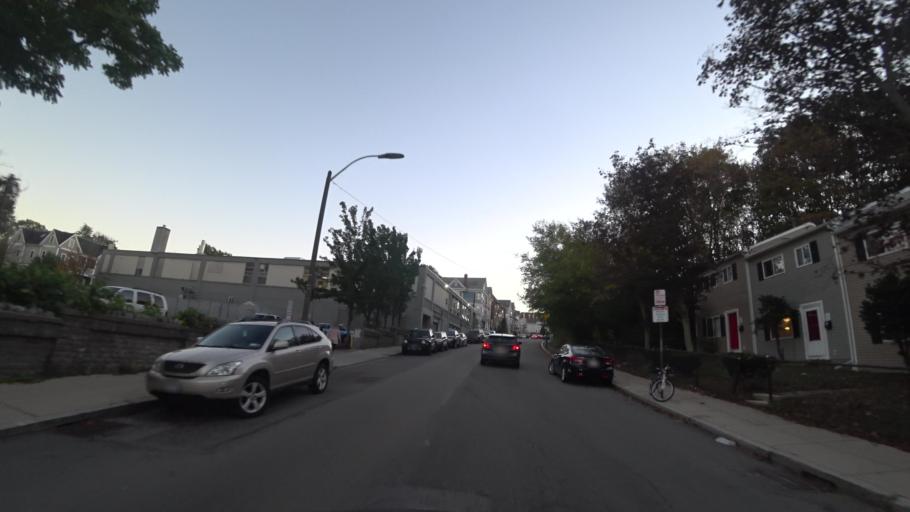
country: US
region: Massachusetts
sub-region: Norfolk County
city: Brookline
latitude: 42.3324
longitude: -71.1017
